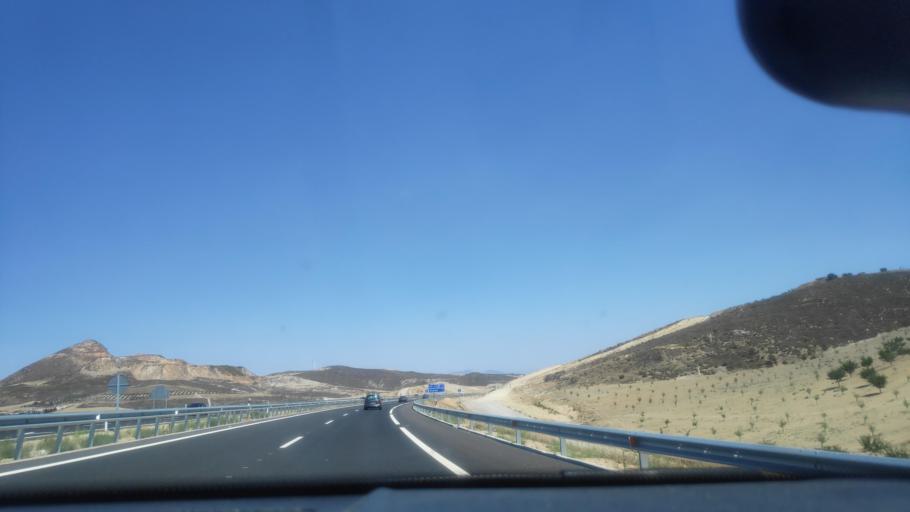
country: ES
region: Andalusia
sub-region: Provincia de Granada
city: Alhendin
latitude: 37.0915
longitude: -3.6718
